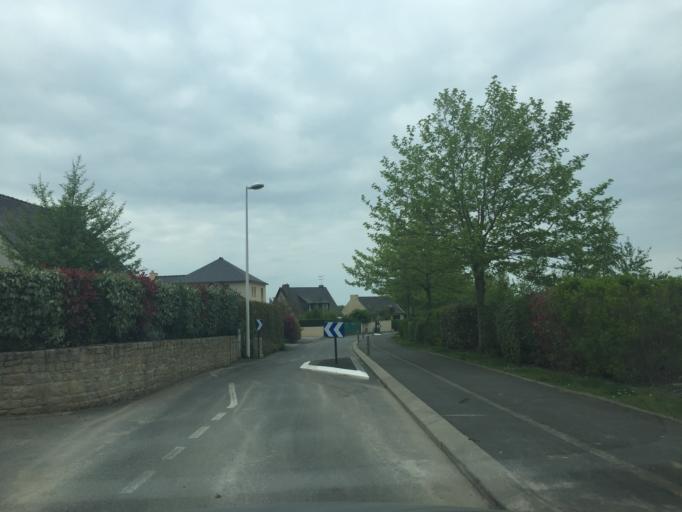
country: FR
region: Brittany
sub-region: Departement des Cotes-d'Armor
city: Matignon
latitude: 48.5979
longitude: -2.2883
